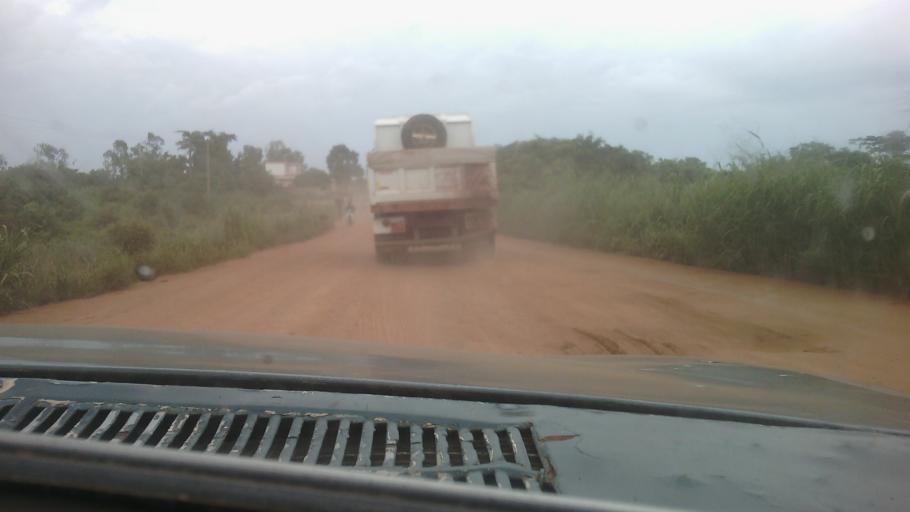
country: BJ
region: Mono
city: Come
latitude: 6.5062
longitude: 1.8327
